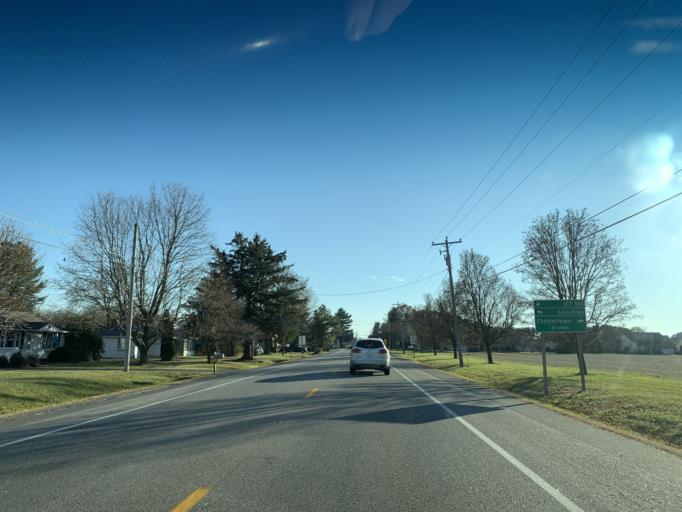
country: US
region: Delaware
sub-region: New Castle County
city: Middletown
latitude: 39.3492
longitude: -75.8782
